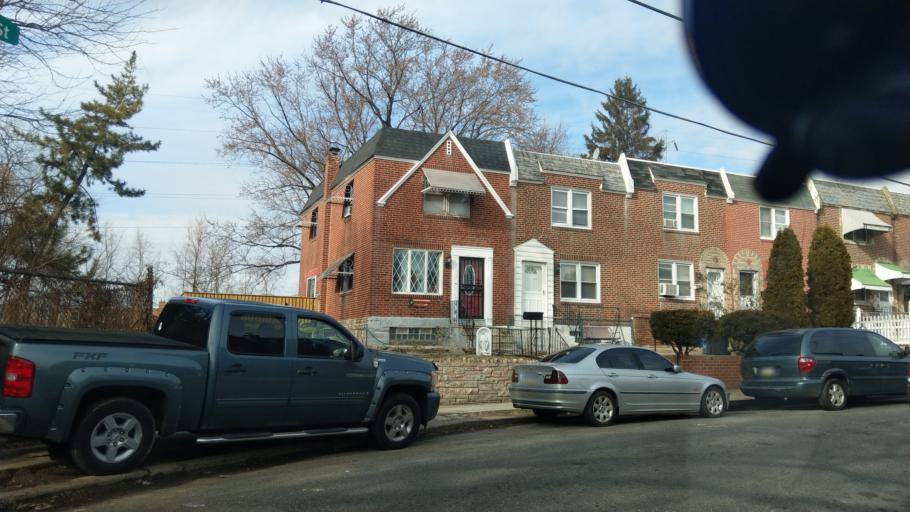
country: US
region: Pennsylvania
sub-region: Montgomery County
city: Rockledge
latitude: 40.0175
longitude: -75.1133
